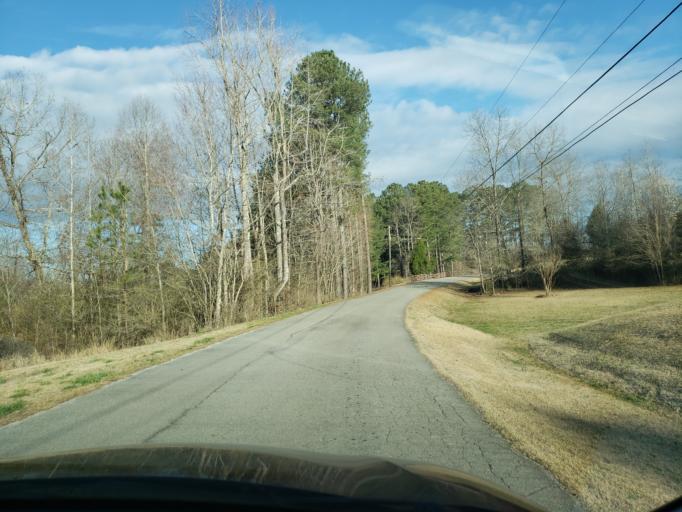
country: US
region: Alabama
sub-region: Cleburne County
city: Heflin
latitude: 33.6355
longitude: -85.6004
